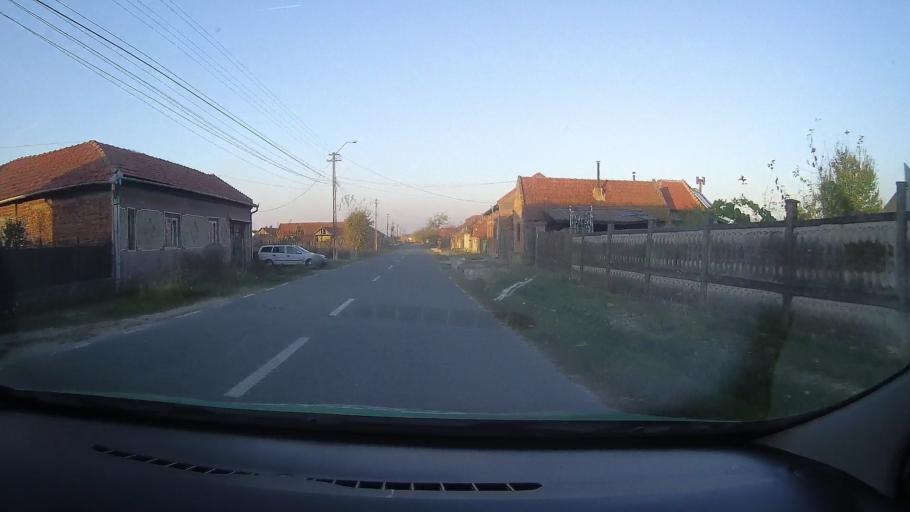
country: RO
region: Timis
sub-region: Comuna Traian Vuia
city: Traian Vuia
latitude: 45.8016
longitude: 22.0241
